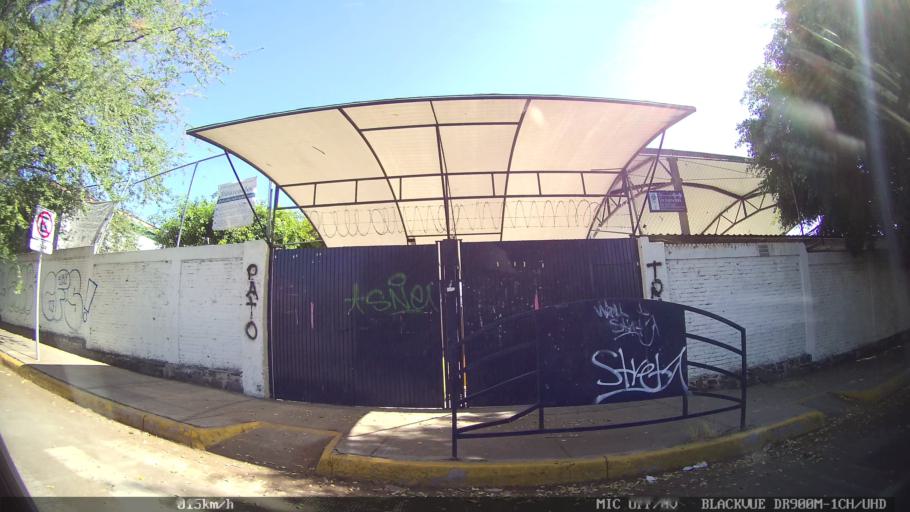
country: MX
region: Jalisco
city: Tlaquepaque
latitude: 20.6831
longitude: -103.2701
